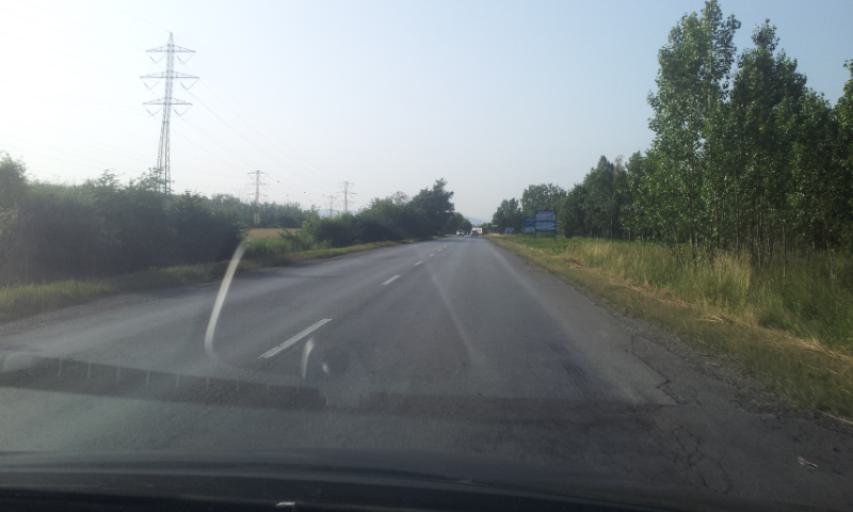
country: SK
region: Kosicky
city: Kosice
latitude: 48.6344
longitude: 21.2126
